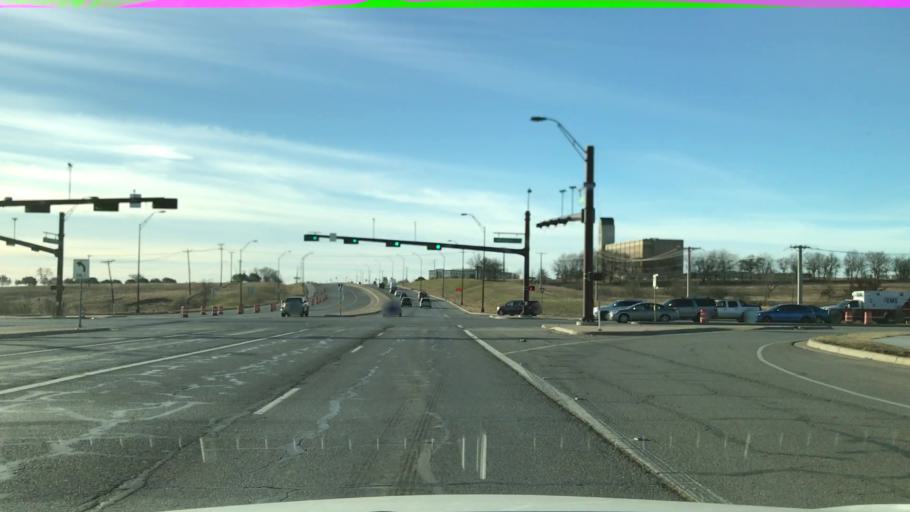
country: US
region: Texas
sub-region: Williamson County
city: Georgetown
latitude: 30.5730
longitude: -97.6507
